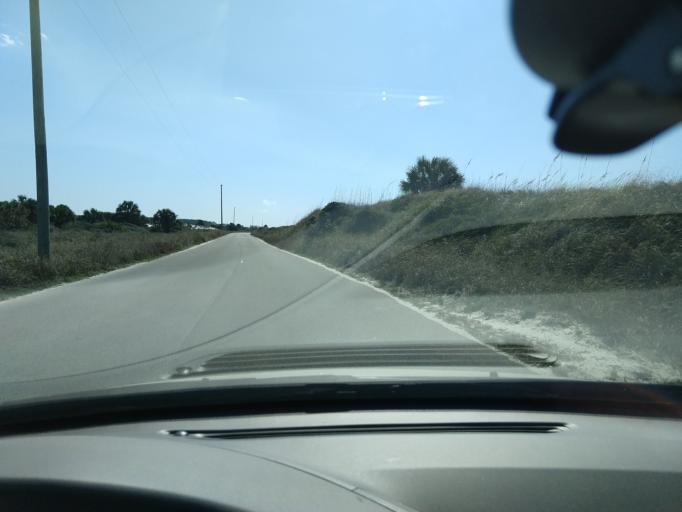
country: US
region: Florida
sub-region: Gulf County
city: Port Saint Joe
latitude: 29.7708
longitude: -85.4048
